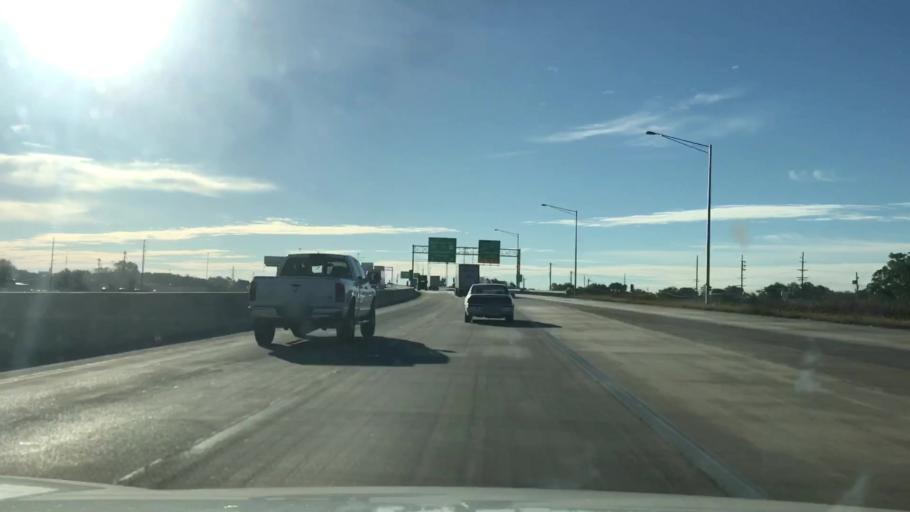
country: US
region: Illinois
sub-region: Saint Clair County
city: East Saint Louis
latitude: 38.6395
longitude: -90.1523
